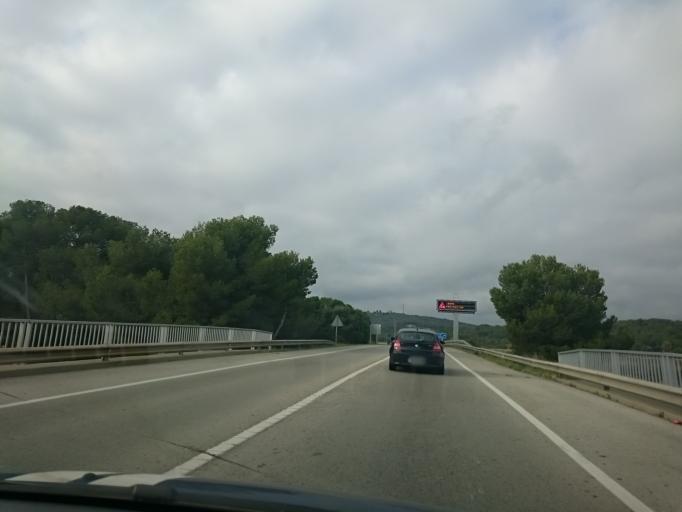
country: ES
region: Catalonia
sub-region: Provincia de Barcelona
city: Sitges
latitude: 41.2414
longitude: 1.8178
